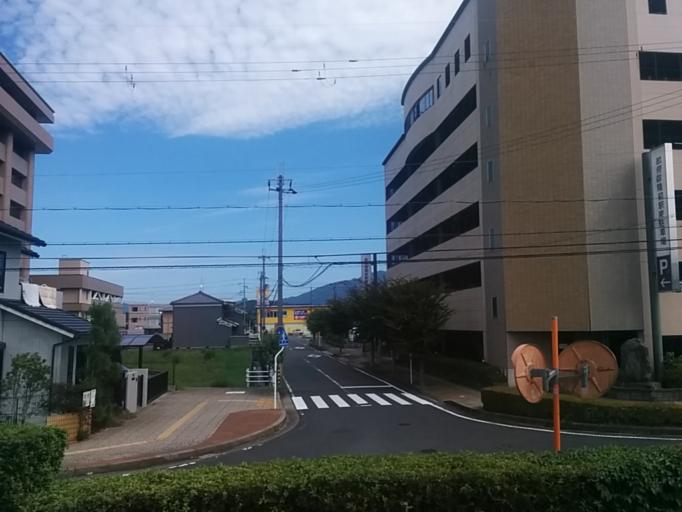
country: JP
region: Nara
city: Kashihara-shi
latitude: 34.4950
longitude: 135.7944
